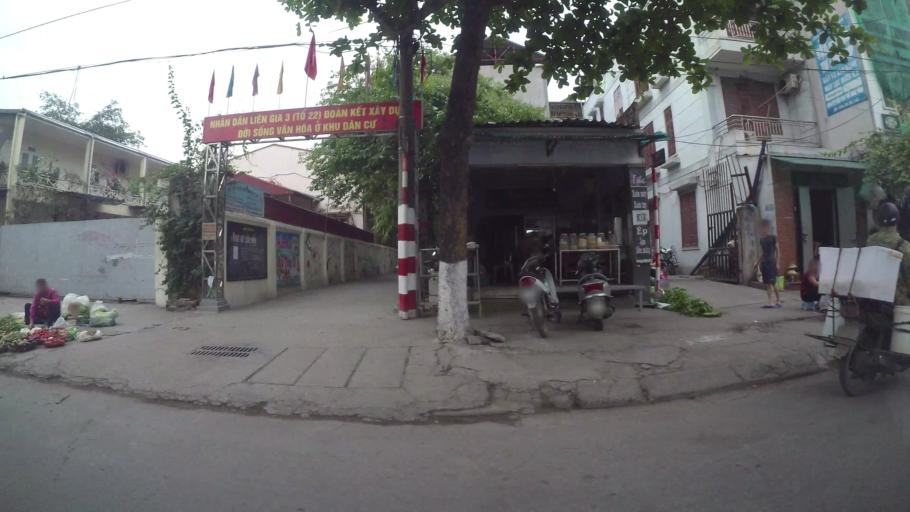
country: VN
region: Ha Noi
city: Hoan Kiem
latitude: 21.0691
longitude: 105.8886
